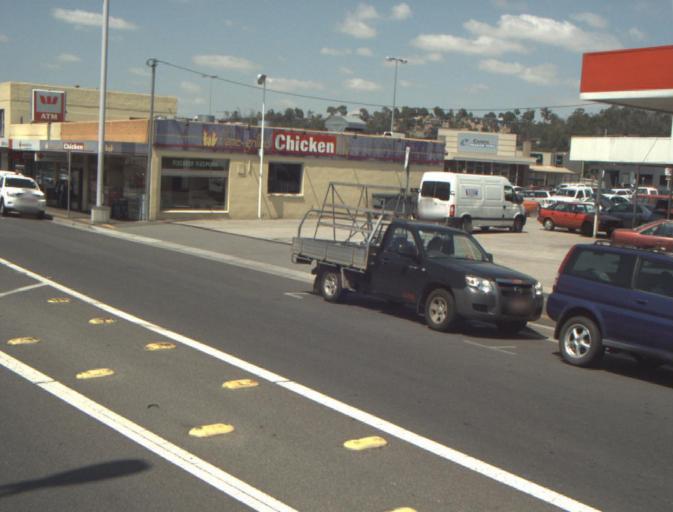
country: AU
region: Tasmania
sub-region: Launceston
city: East Launceston
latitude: -41.4655
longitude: 147.1593
